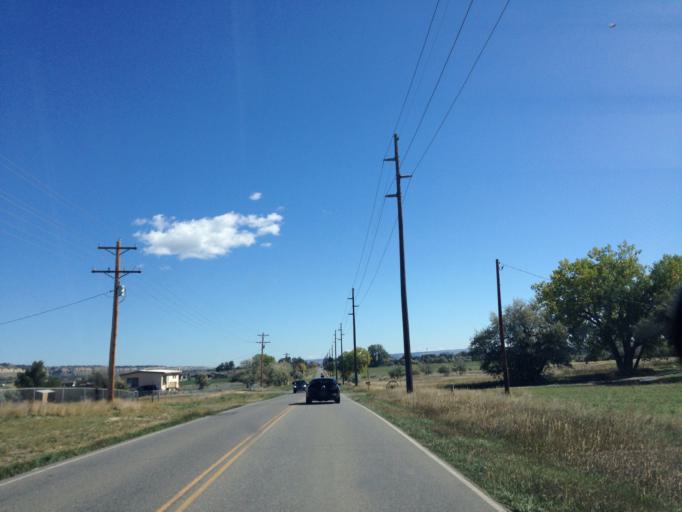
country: US
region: Montana
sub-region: Yellowstone County
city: Laurel
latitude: 45.7840
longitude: -108.6773
